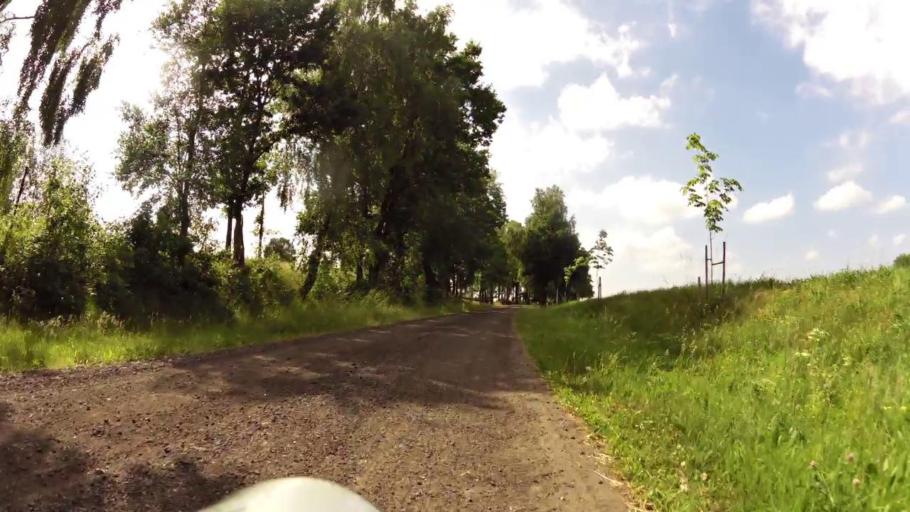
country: PL
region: West Pomeranian Voivodeship
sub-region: Powiat koszalinski
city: Bobolice
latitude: 53.9499
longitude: 16.6280
